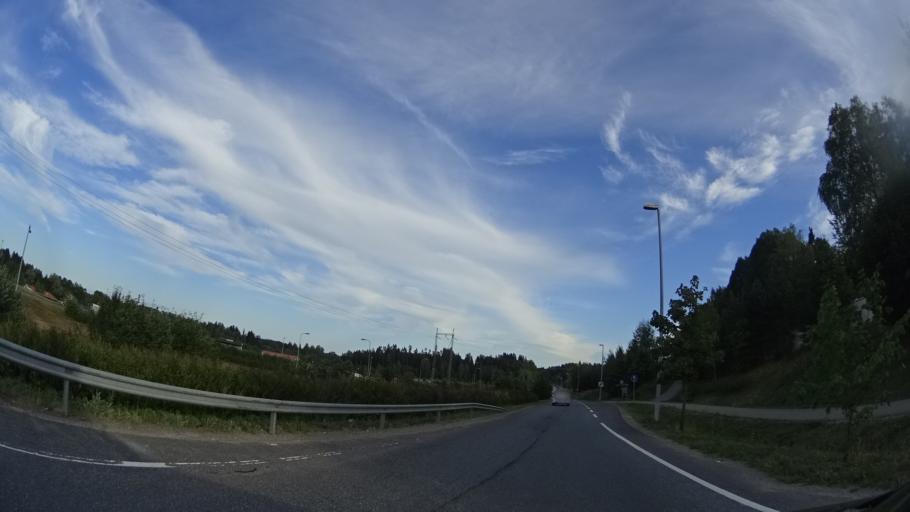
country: FI
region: Uusimaa
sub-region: Helsinki
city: Vihti
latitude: 60.3315
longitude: 24.3315
